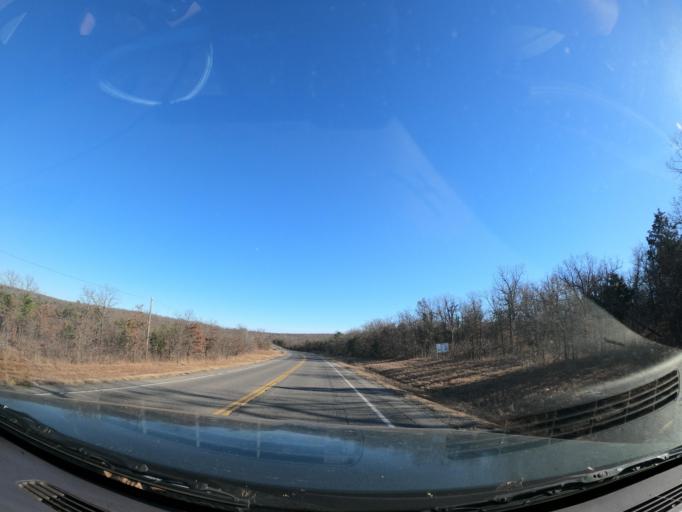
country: US
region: Oklahoma
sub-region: Pittsburg County
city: Longtown
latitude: 35.2270
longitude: -95.4489
